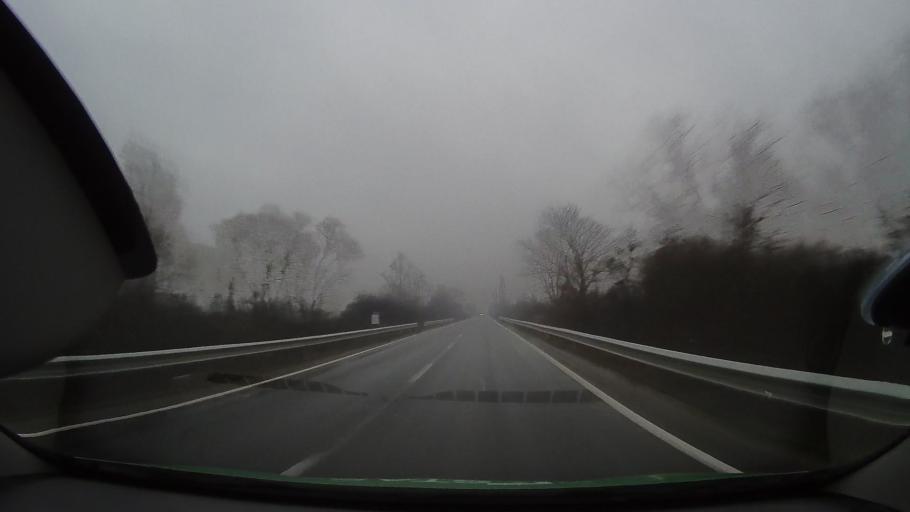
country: RO
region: Bihor
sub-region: Comuna Tinca
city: Tinca
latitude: 46.7586
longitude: 21.9354
